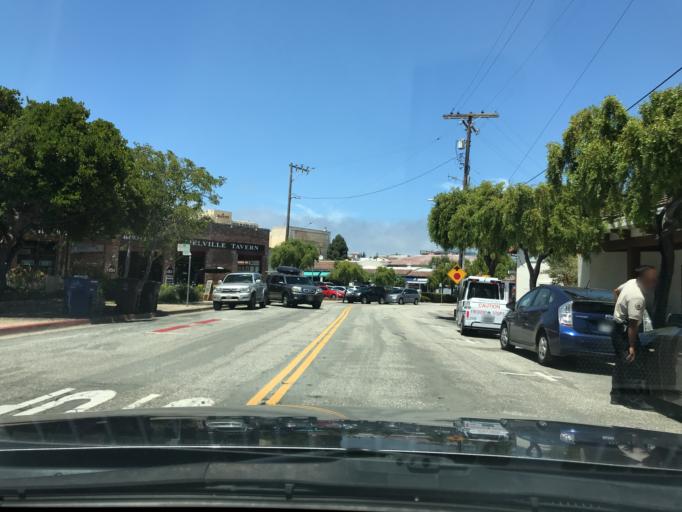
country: US
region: California
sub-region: Monterey County
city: Monterey
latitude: 36.5979
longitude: -121.8928
